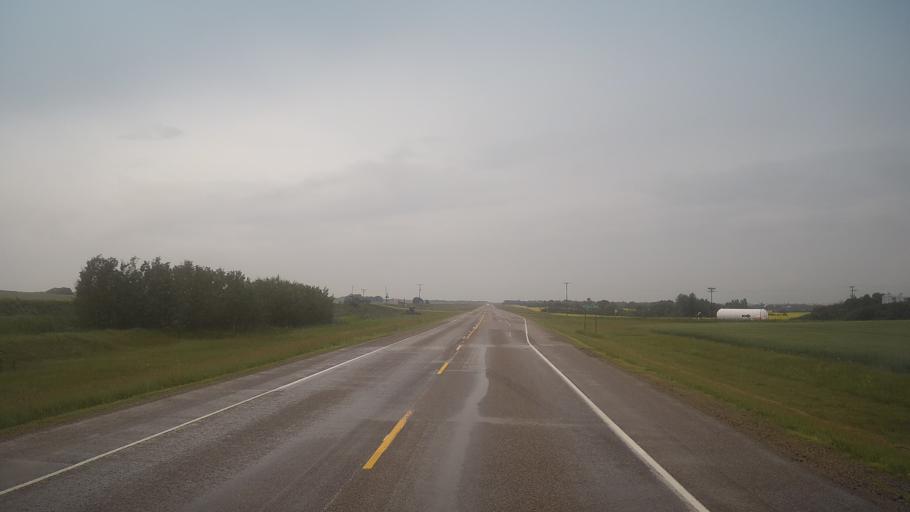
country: CA
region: Saskatchewan
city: Wilkie
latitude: 52.2296
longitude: -108.5378
